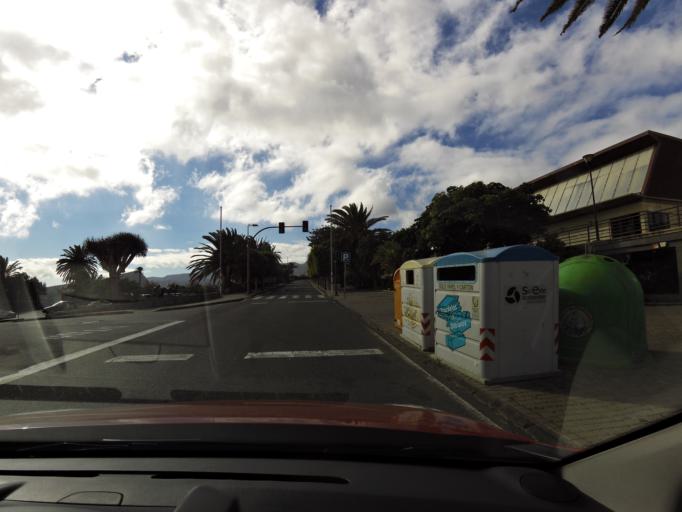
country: ES
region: Canary Islands
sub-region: Provincia de Las Palmas
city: Aguimes
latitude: 27.9040
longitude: -15.4482
